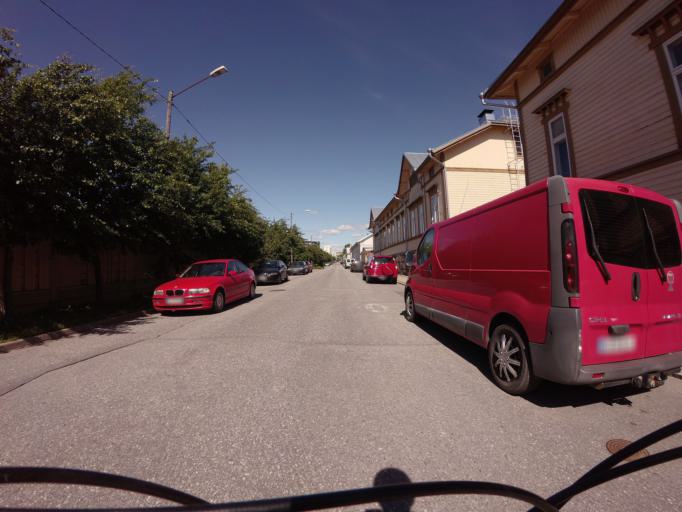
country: FI
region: Varsinais-Suomi
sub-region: Turku
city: Turku
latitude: 60.4481
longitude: 22.2413
